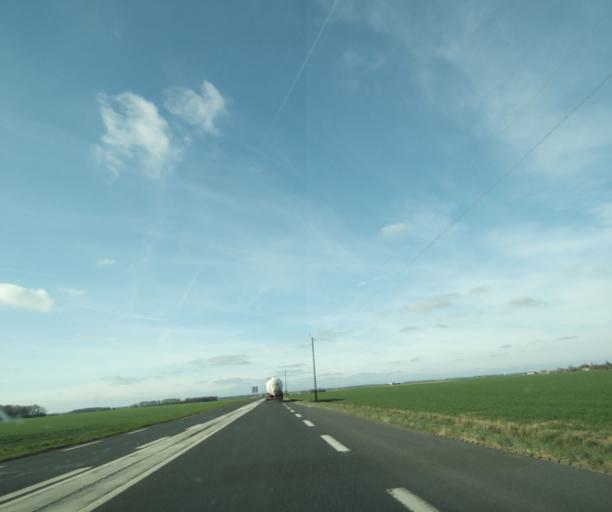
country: FR
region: Ile-de-France
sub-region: Departement des Yvelines
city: Ablis
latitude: 48.4850
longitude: 1.8481
